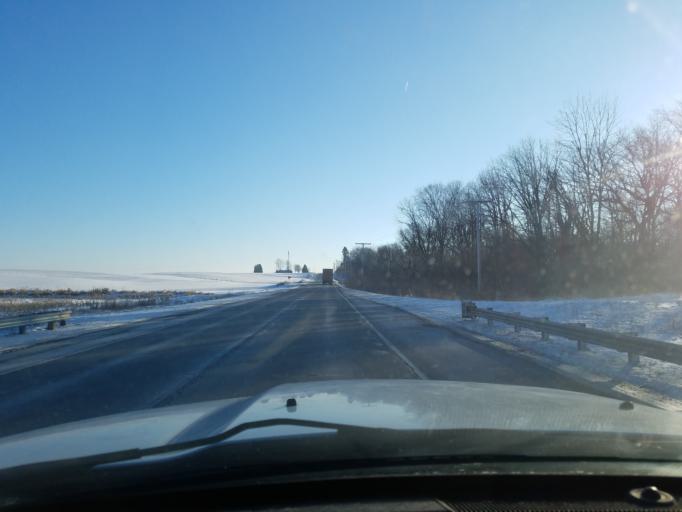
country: US
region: Indiana
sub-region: Noble County
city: Albion
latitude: 41.4531
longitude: -85.4583
